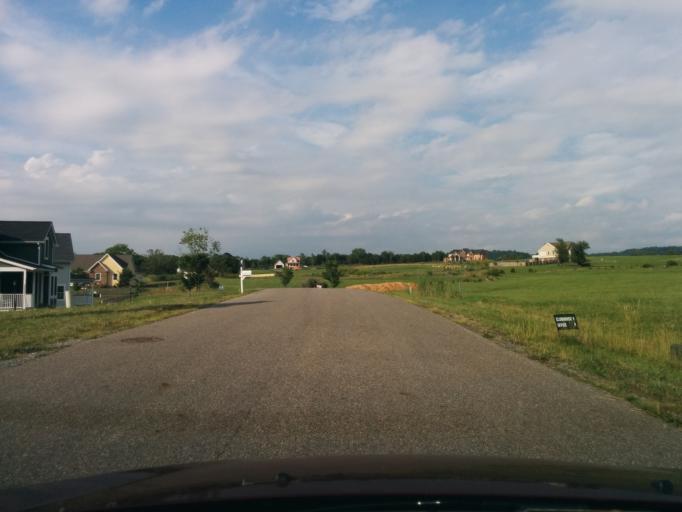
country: US
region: Virginia
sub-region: Rockbridge County
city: East Lexington
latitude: 37.7912
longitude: -79.4082
